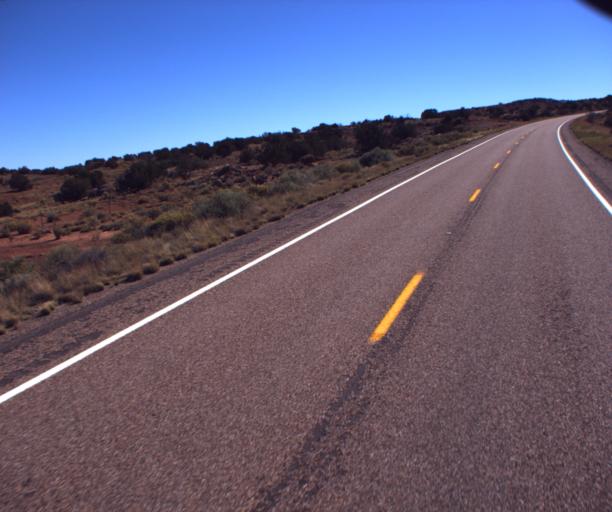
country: US
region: Arizona
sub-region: Apache County
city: Saint Johns
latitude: 34.5862
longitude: -109.5435
